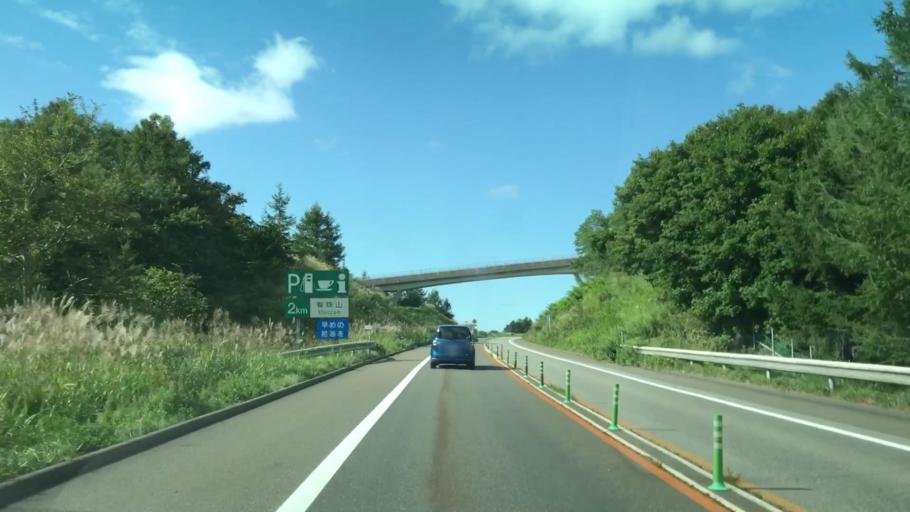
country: JP
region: Hokkaido
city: Date
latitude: 42.4447
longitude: 140.9149
